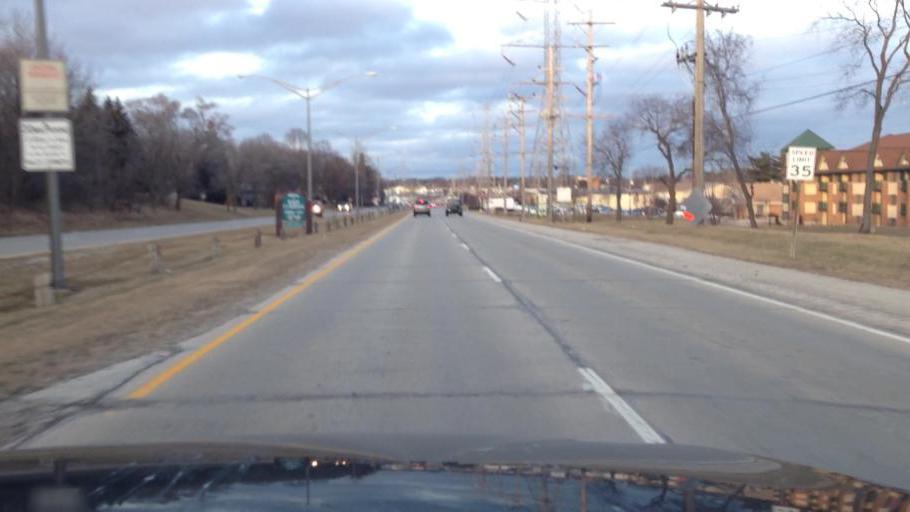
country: US
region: Wisconsin
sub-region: Milwaukee County
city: Hales Corners
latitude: 42.9302
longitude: -88.0525
